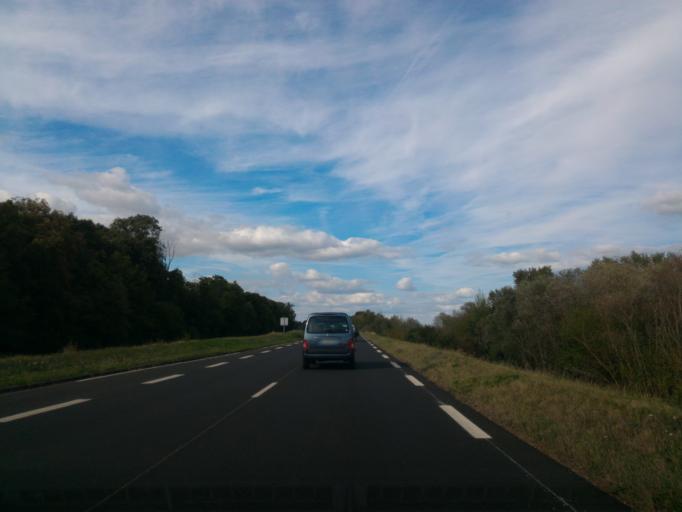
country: FR
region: Centre
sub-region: Departement du Loir-et-Cher
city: Chailles
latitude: 47.5449
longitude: 1.2859
